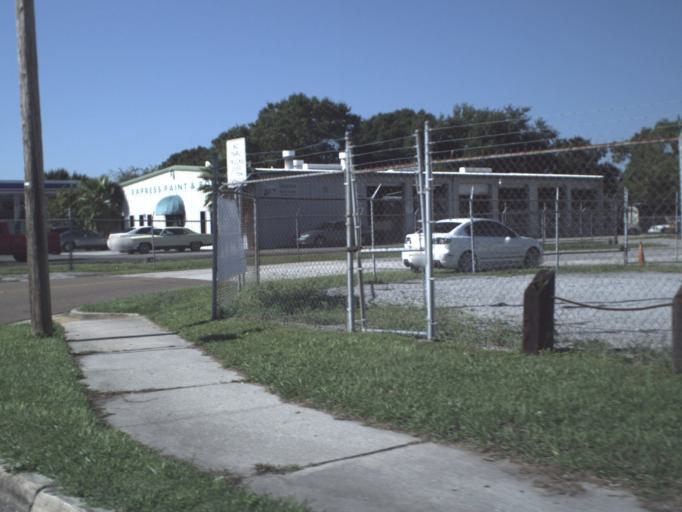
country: US
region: Florida
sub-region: Polk County
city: Winston
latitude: 28.0502
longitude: -81.9902
